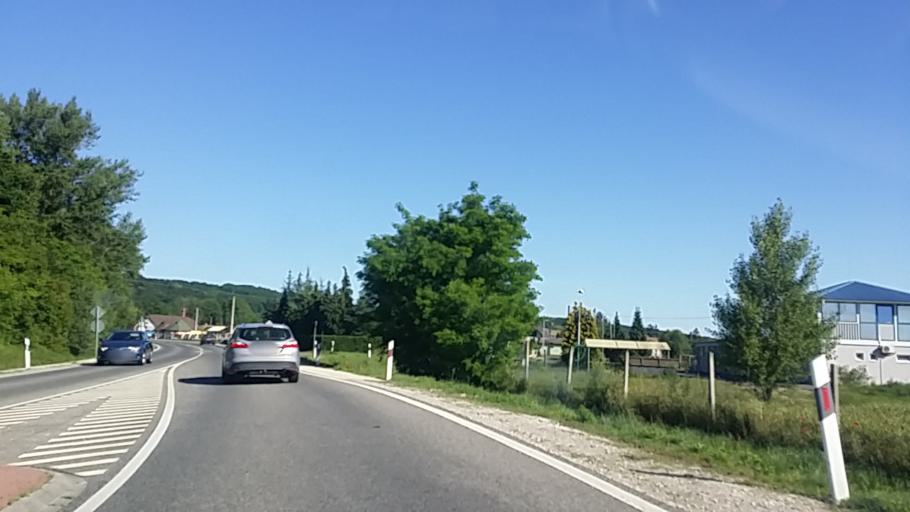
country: HU
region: Zala
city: Heviz
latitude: 46.8040
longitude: 17.1019
